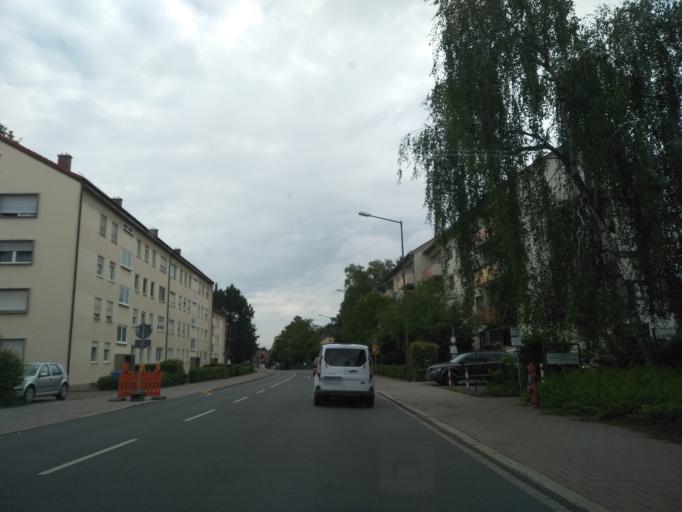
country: DE
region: Bavaria
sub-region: Regierungsbezirk Mittelfranken
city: Erlangen
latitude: 49.5800
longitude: 11.0056
